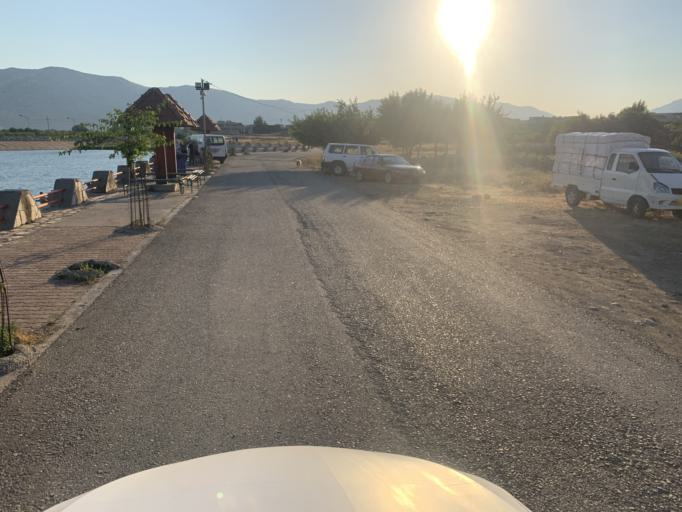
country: IQ
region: As Sulaymaniyah
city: Raniye
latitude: 36.2734
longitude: 44.7524
